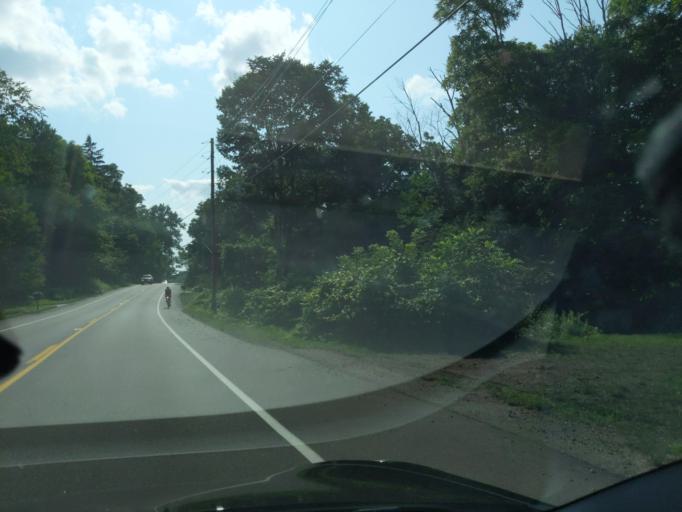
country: US
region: Michigan
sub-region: Kent County
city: Lowell
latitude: 42.9230
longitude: -85.3466
